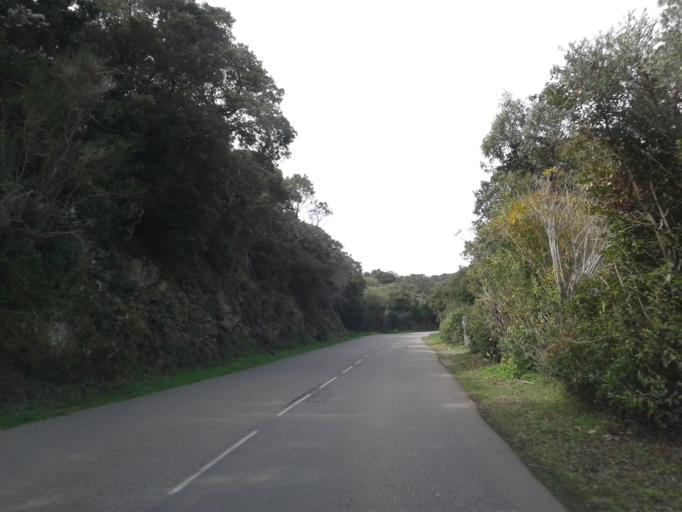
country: FR
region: Corsica
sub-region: Departement de la Haute-Corse
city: Brando
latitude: 42.9476
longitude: 9.4589
